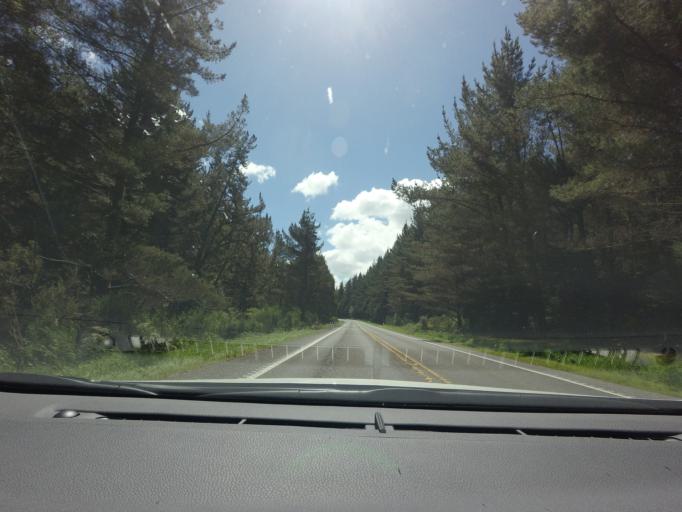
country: NZ
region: Bay of Plenty
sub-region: Rotorua District
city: Rotorua
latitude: -38.1872
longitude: 176.2573
